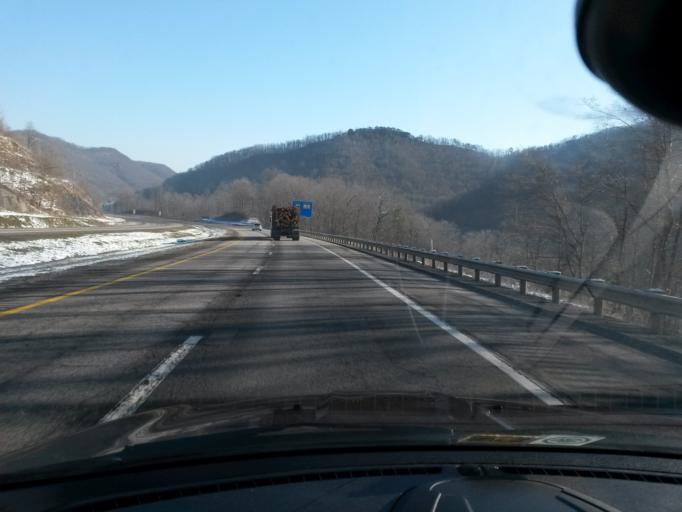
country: US
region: West Virginia
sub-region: Nicholas County
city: Craigsville
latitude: 38.4836
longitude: -80.7597
